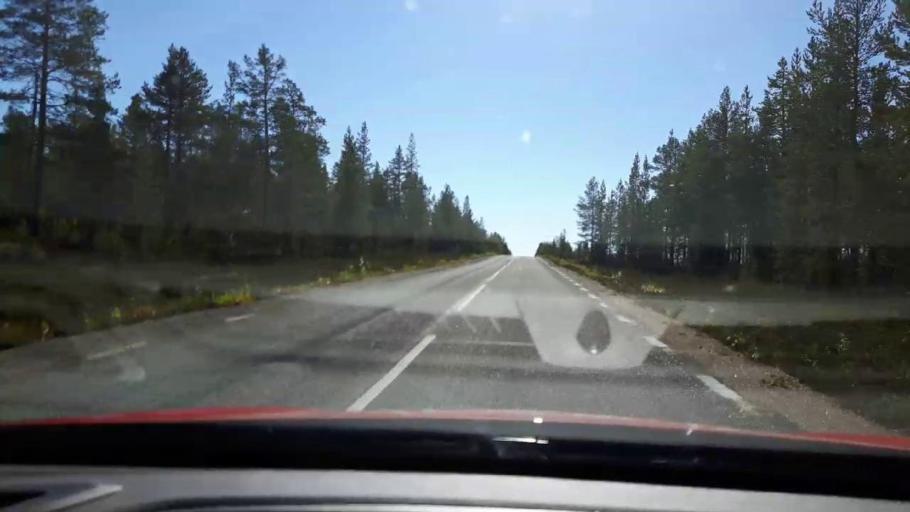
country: SE
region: Jaemtland
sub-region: Harjedalens Kommun
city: Sveg
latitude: 61.7330
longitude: 14.1642
